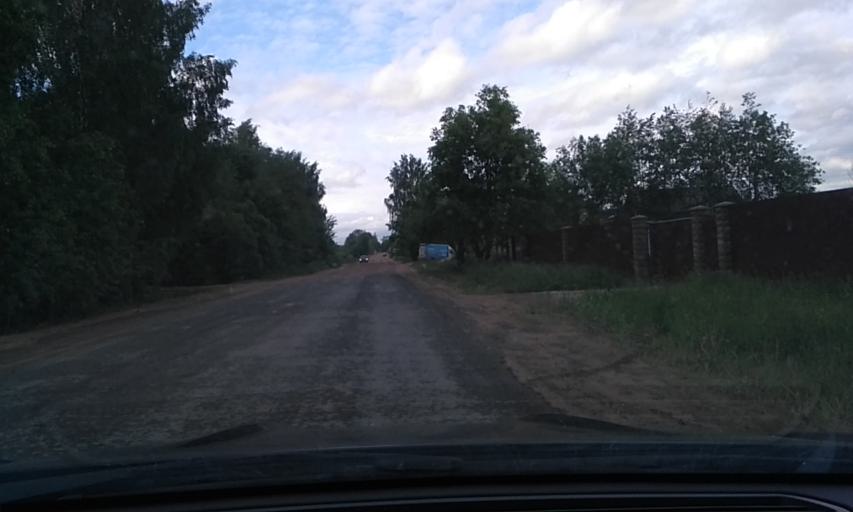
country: RU
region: Leningrad
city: Otradnoye
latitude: 59.7913
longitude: 30.7935
